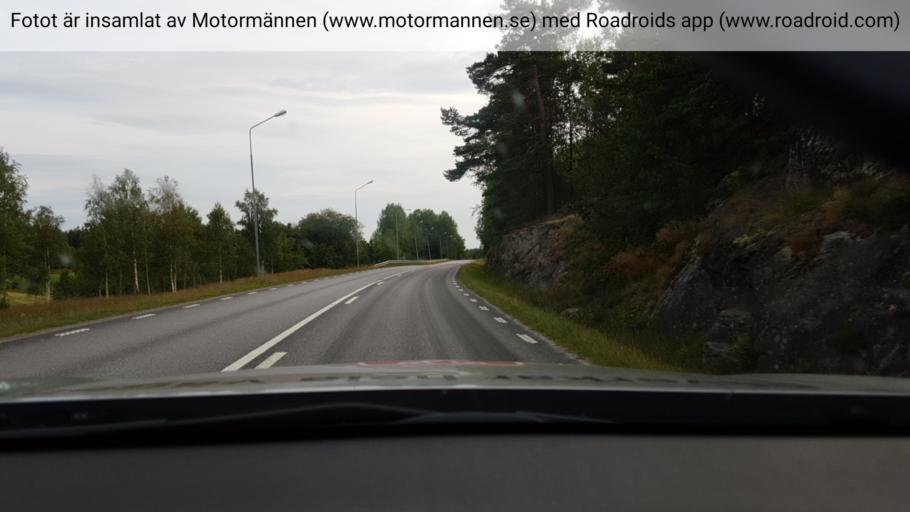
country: SE
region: Vaestra Goetaland
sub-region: Uddevalla Kommun
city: Uddevalla
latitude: 58.4167
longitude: 12.0190
